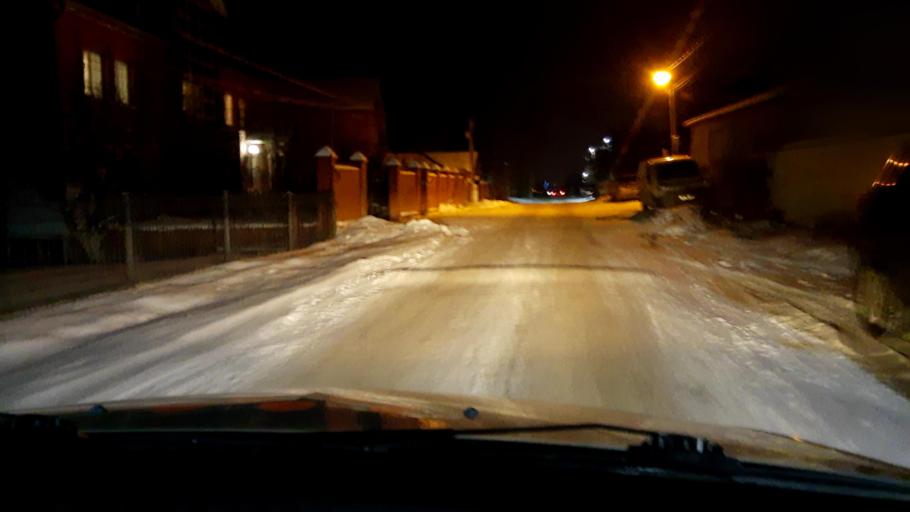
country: RU
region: Bashkortostan
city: Mikhaylovka
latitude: 54.8143
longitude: 55.8993
